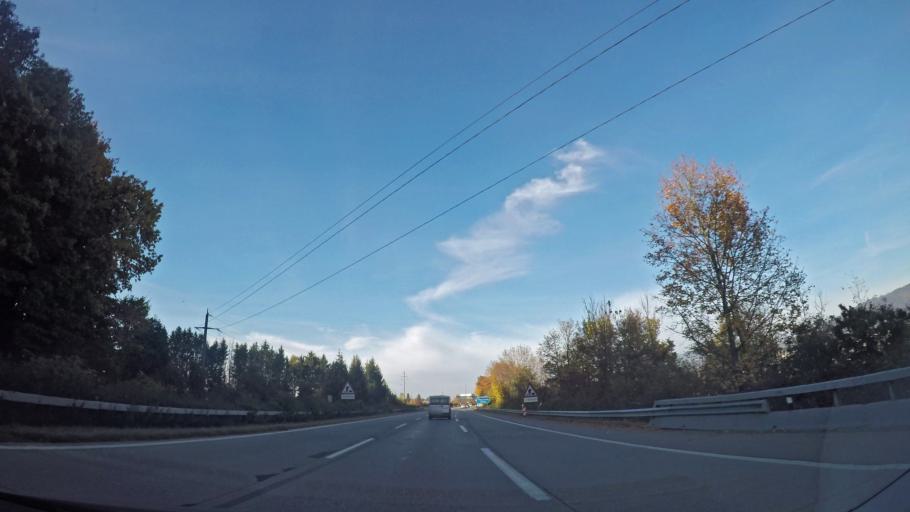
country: CH
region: Bern
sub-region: Thun District
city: Thun
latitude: 46.7346
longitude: 7.6008
